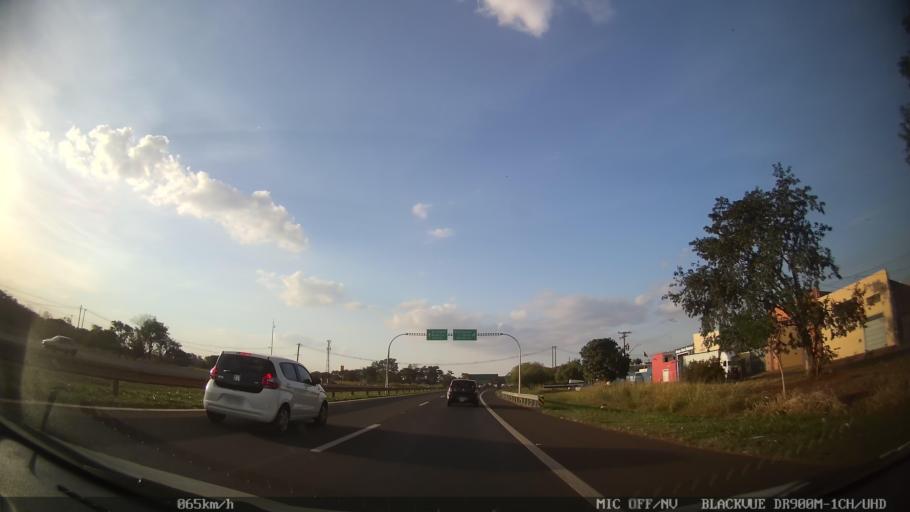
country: BR
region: Sao Paulo
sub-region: Ribeirao Preto
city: Ribeirao Preto
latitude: -21.1196
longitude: -47.7857
